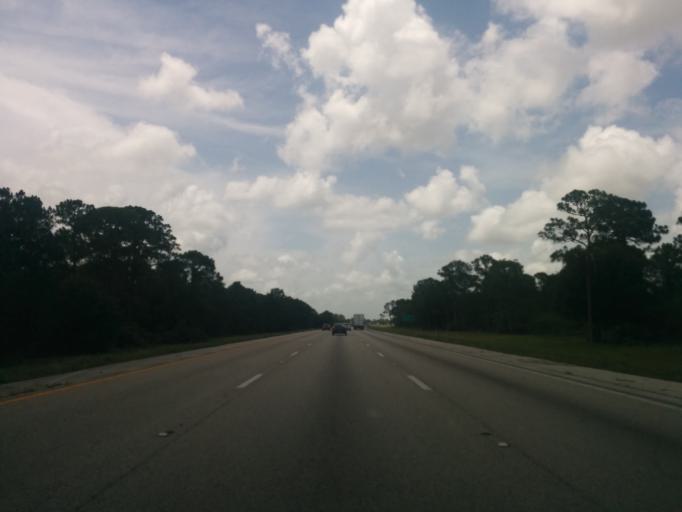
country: US
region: Florida
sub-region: Martin County
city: Palm City
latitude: 27.1734
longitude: -80.3942
